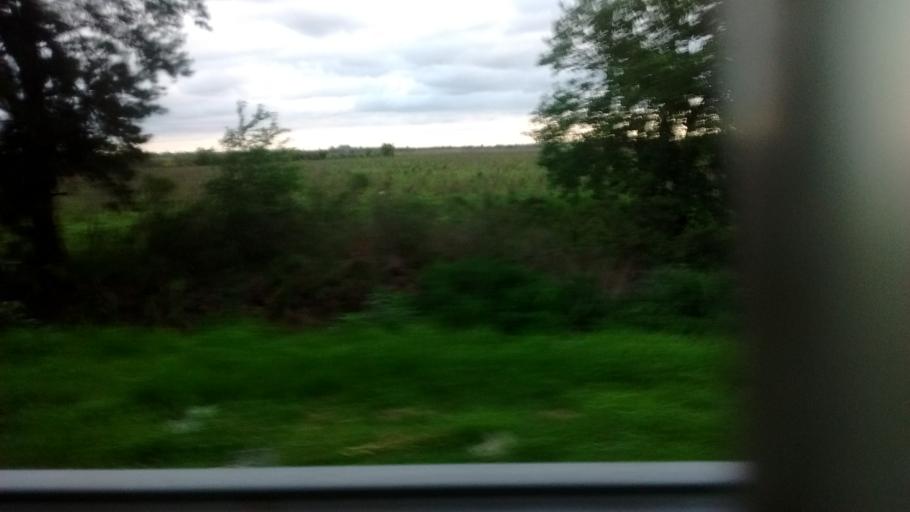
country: AR
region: Santa Fe
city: Funes
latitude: -32.9278
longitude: -60.7733
